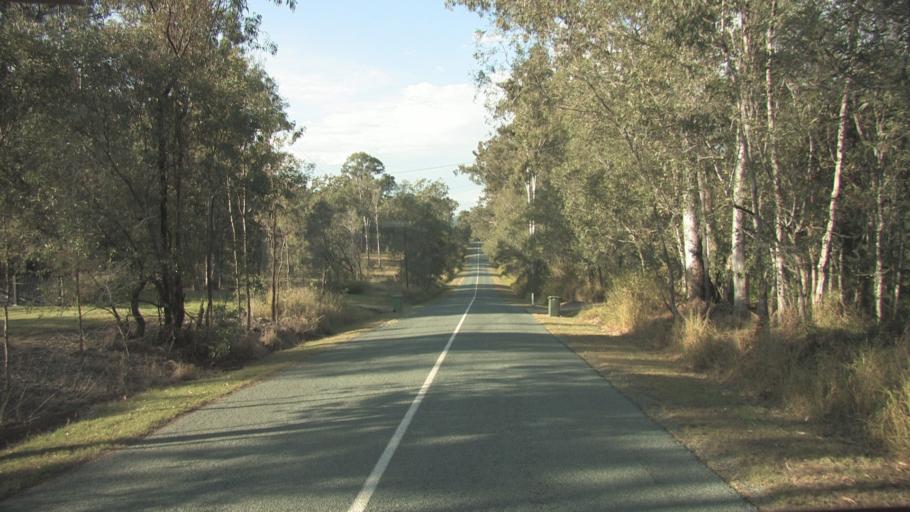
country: AU
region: Queensland
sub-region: Gold Coast
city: Ormeau Hills
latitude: -27.8410
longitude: 153.1629
